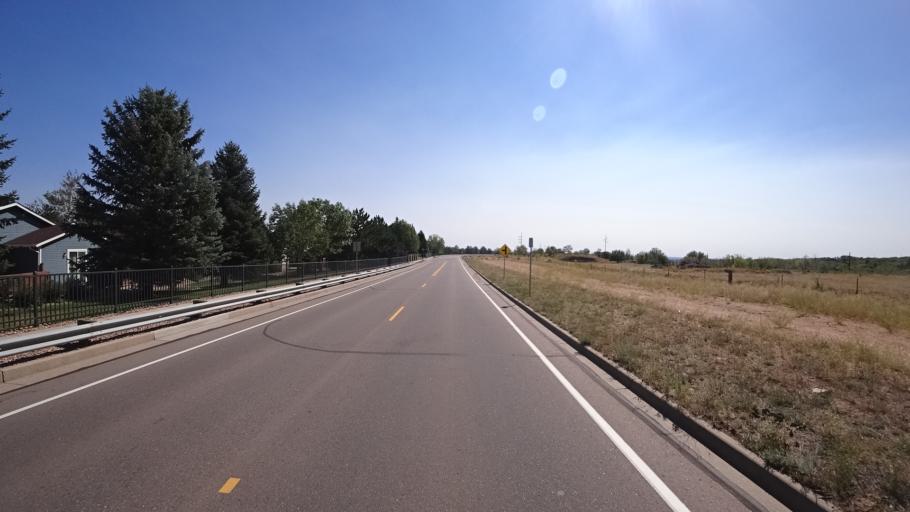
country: US
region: Colorado
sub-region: El Paso County
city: Colorado Springs
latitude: 38.8305
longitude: -104.8731
